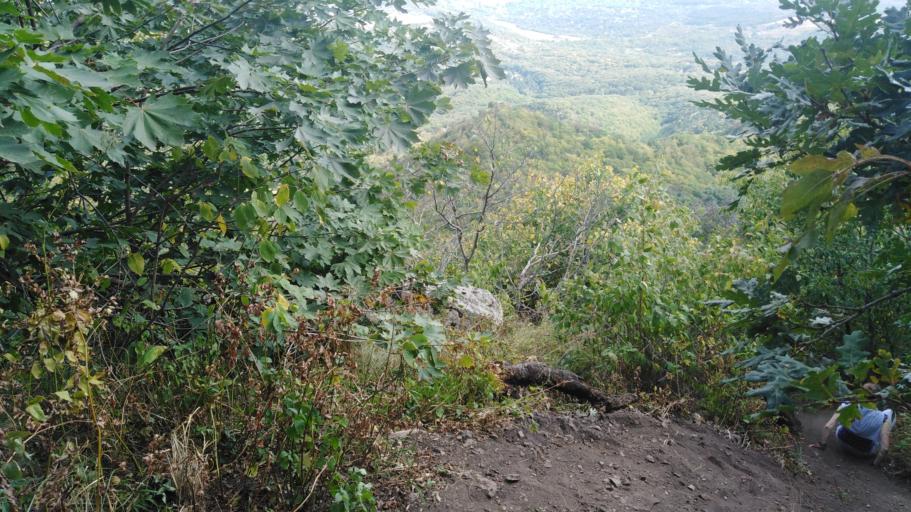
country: RU
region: Stavropol'skiy
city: Zheleznovodsk
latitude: 44.0970
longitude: 43.0274
